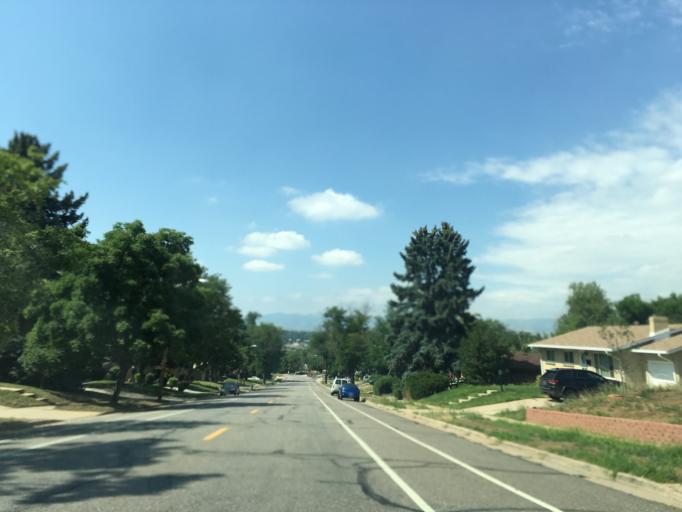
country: US
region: Colorado
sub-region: Arapahoe County
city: Sheridan
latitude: 39.6661
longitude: -105.0421
